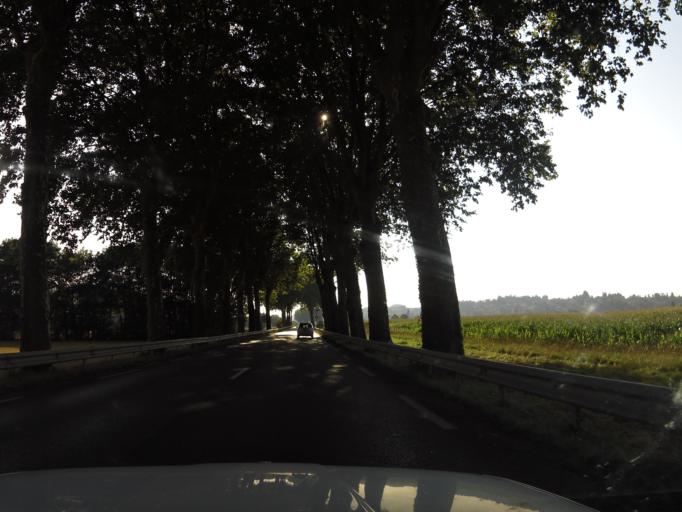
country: FR
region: Rhone-Alpes
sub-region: Departement de l'Ain
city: Meximieux
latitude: 45.9062
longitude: 5.2209
